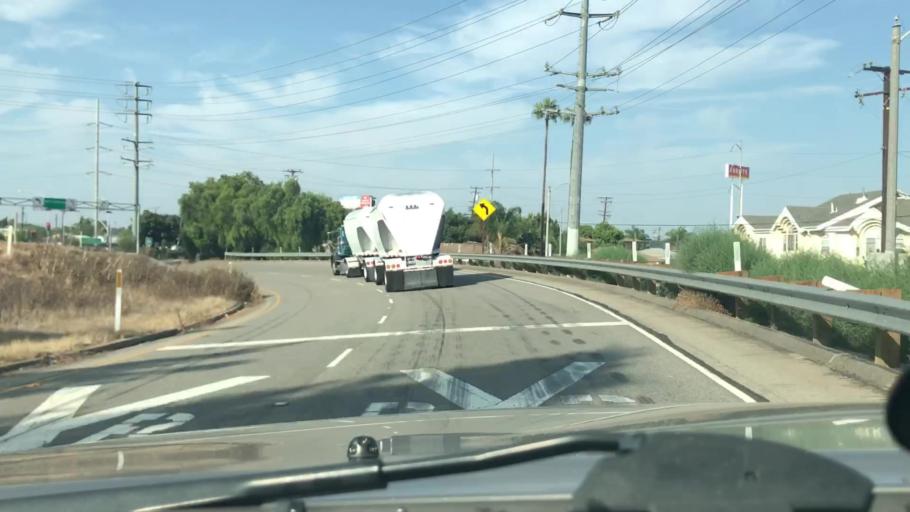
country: US
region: California
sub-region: Los Angeles County
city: Del Aire
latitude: 33.9149
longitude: -118.3690
